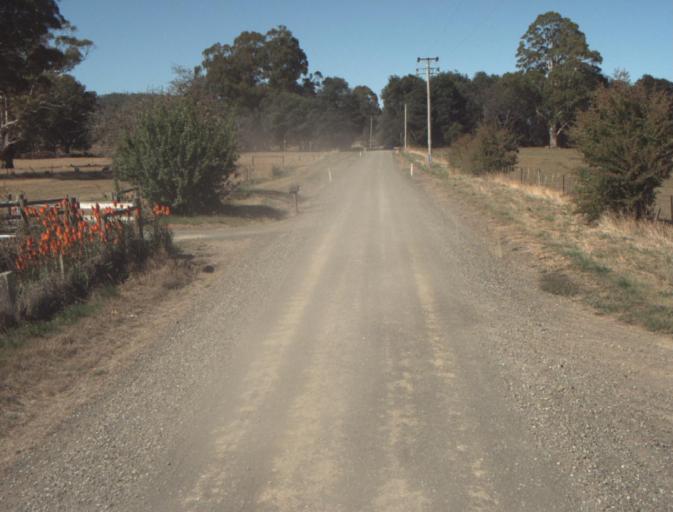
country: AU
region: Tasmania
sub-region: Launceston
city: Newstead
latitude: -41.3156
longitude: 147.3204
